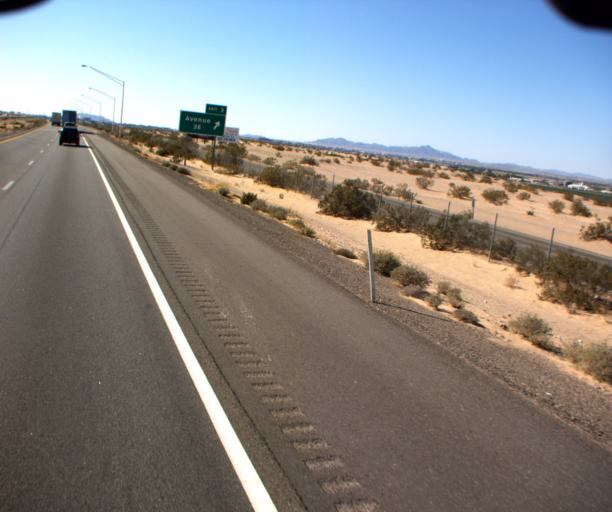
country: US
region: Arizona
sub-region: Yuma County
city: Yuma
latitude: 32.6871
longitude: -114.5709
